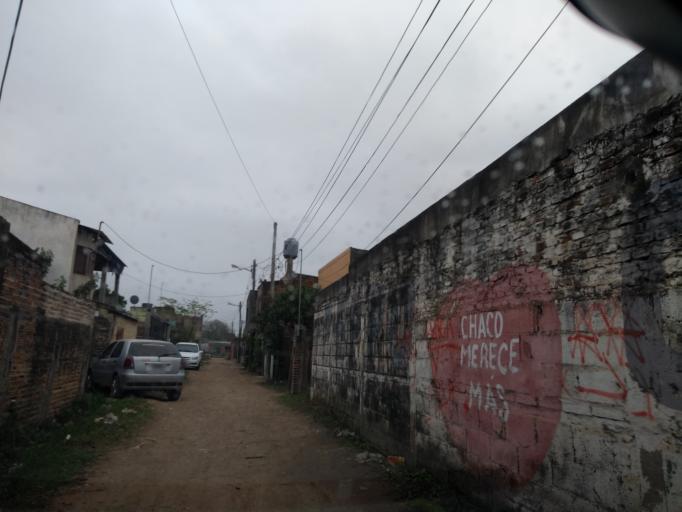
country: AR
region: Chaco
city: Resistencia
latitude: -27.4784
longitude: -58.9759
